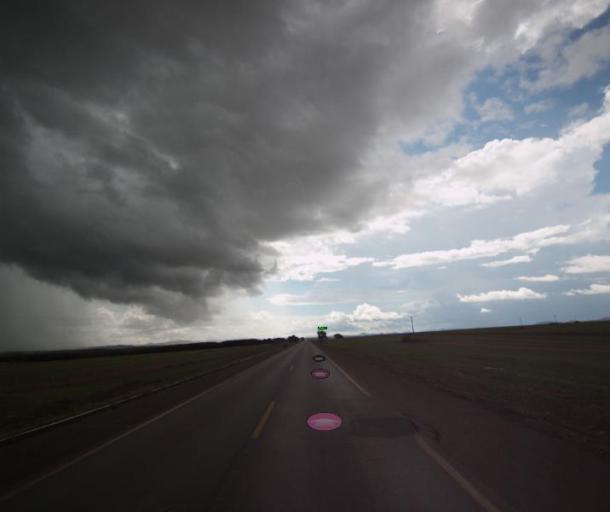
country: BR
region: Goias
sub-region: Uruacu
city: Uruacu
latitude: -14.6431
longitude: -49.1715
